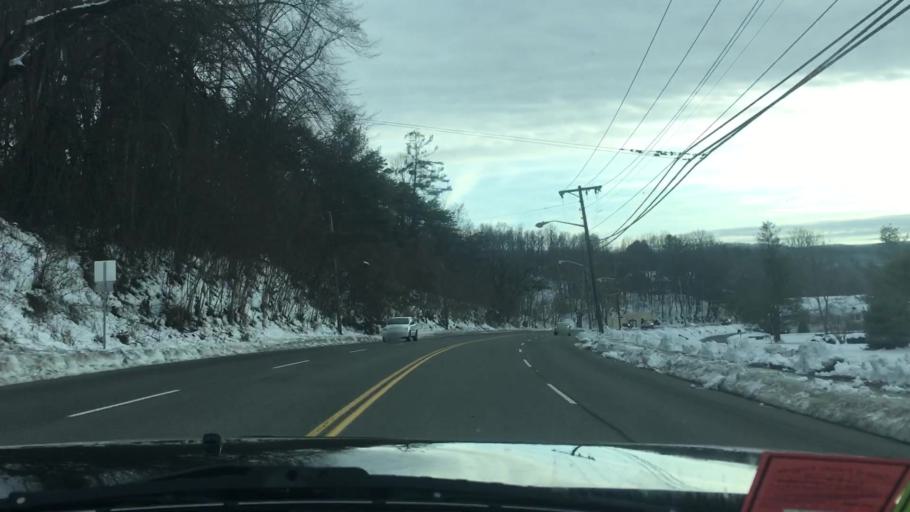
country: US
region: Virginia
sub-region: Pulaski County
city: Pulaski
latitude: 37.0586
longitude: -80.7719
